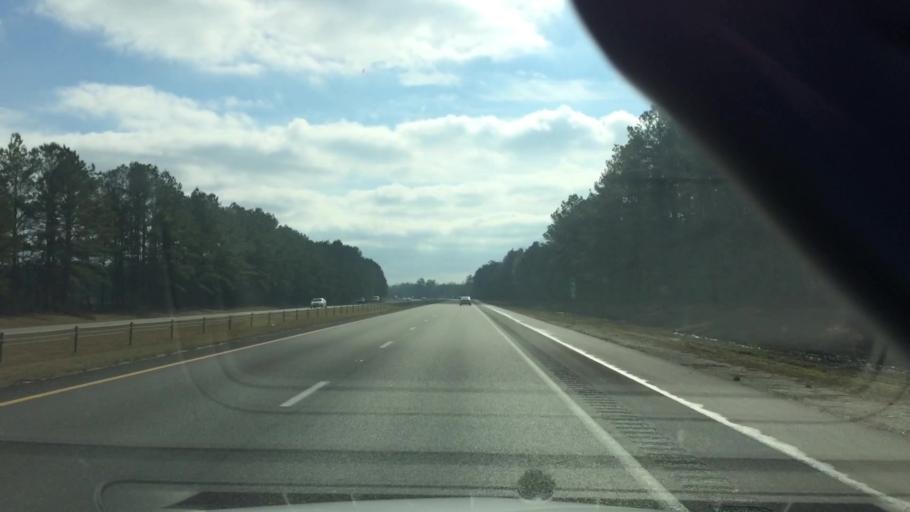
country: US
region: North Carolina
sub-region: Pender County
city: Rocky Point
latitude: 34.4707
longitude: -77.8798
